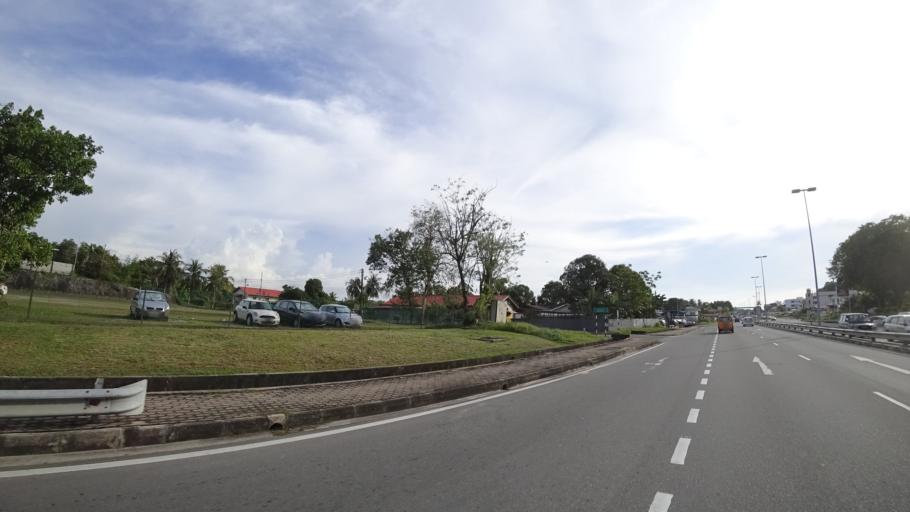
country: BN
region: Brunei and Muara
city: Bandar Seri Begawan
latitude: 4.8567
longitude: 114.8923
